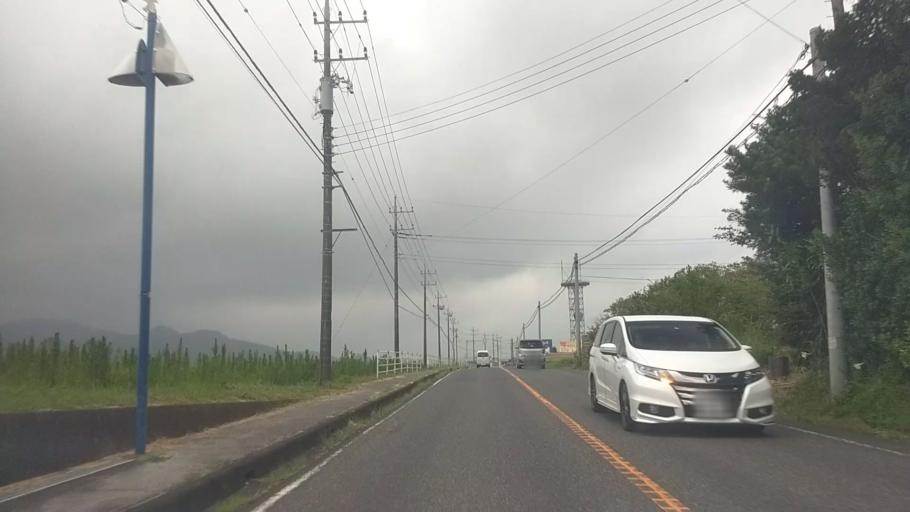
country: JP
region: Chiba
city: Kawaguchi
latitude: 35.1297
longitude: 140.0297
